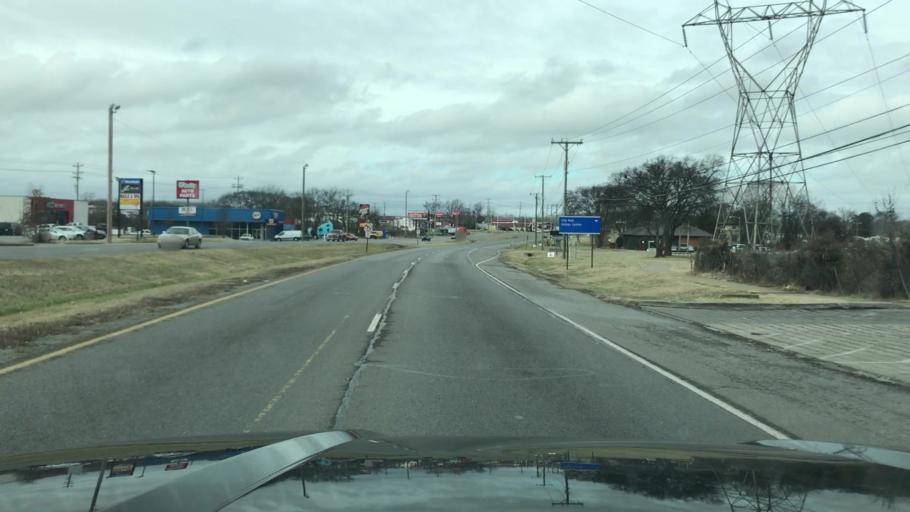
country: US
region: Tennessee
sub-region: Rutherford County
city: La Vergne
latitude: 36.0210
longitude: -86.5795
